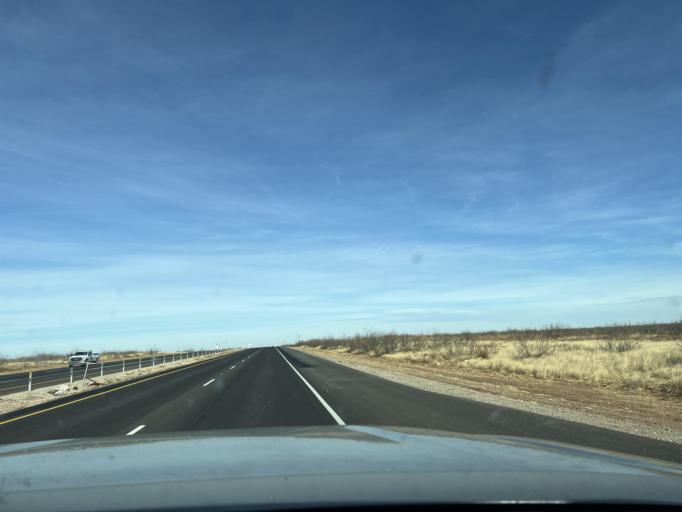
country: US
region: Texas
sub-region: Ector County
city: Gardendale
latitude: 32.0889
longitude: -102.4512
